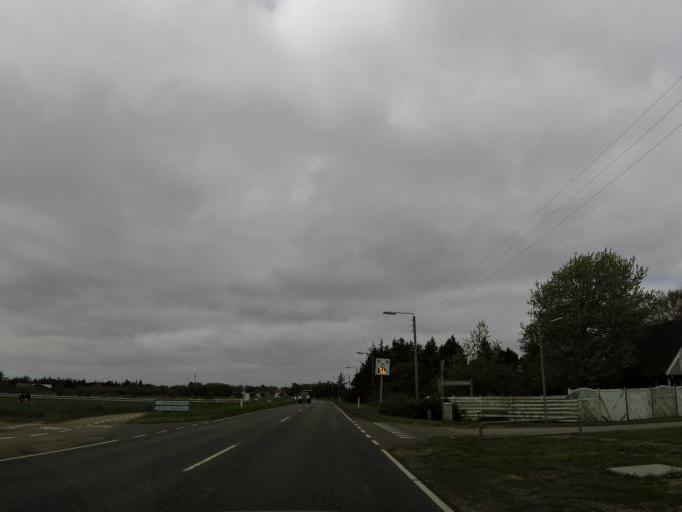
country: DE
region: Schleswig-Holstein
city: List
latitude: 55.1259
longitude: 8.5498
